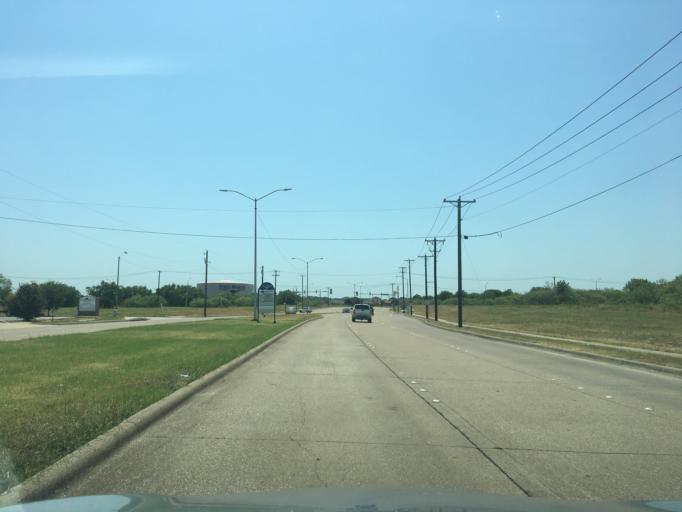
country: US
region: Texas
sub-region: Tarrant County
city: Crowley
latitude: 32.6168
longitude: -97.3708
